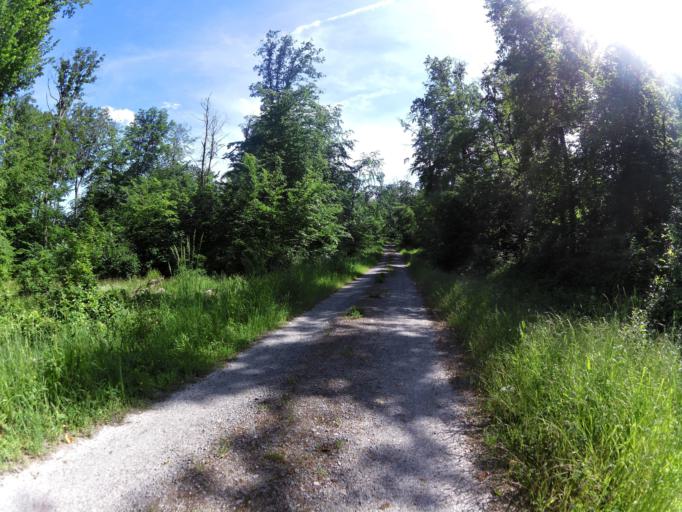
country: DE
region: Bavaria
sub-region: Regierungsbezirk Unterfranken
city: Uettingen
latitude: 49.7825
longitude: 9.7379
